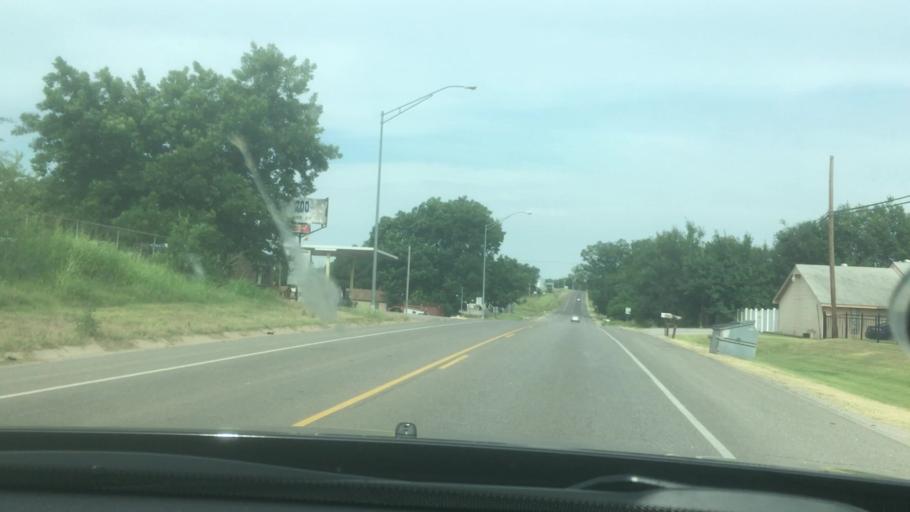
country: US
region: Oklahoma
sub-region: Garvin County
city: Maysville
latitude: 34.8173
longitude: -97.4194
